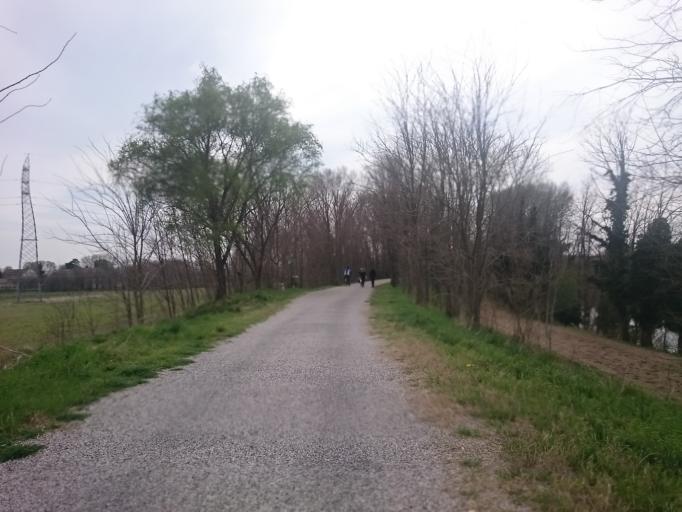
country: IT
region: Veneto
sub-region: Provincia di Padova
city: Saletto
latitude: 45.4592
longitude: 11.8645
